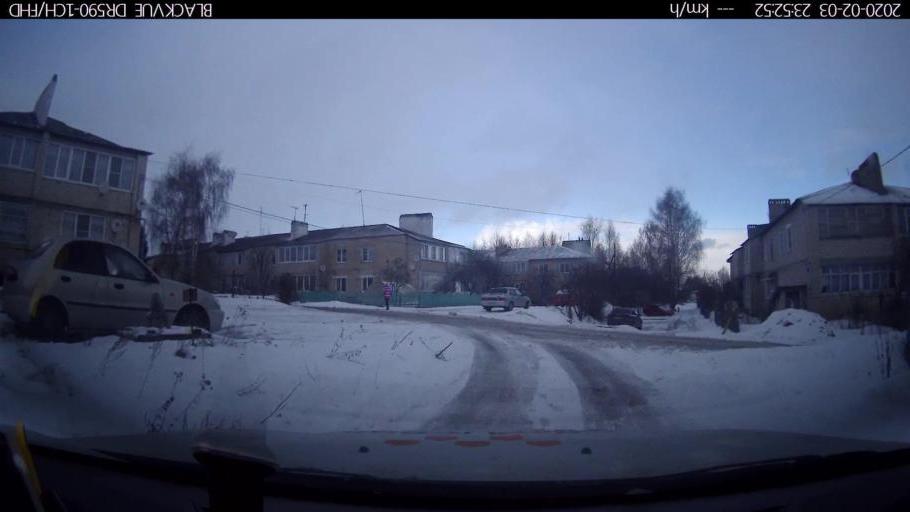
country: RU
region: Nizjnij Novgorod
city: Dal'neye Konstantinovo
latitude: 55.8055
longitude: 44.0789
